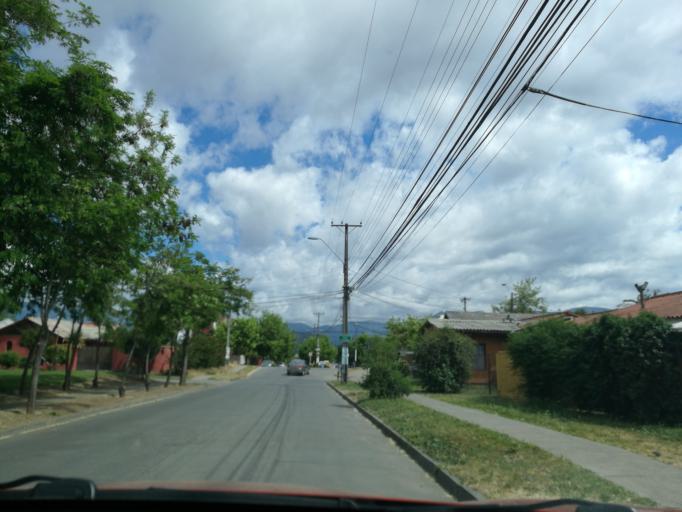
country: CL
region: O'Higgins
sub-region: Provincia de Cachapoal
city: Rancagua
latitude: -34.1331
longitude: -70.7364
